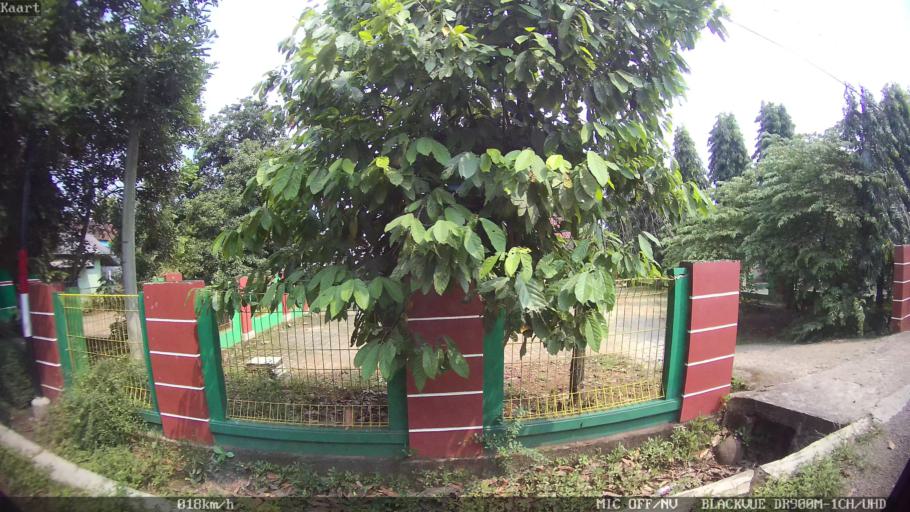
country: ID
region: Lampung
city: Gadingrejo
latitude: -5.3622
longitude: 105.0436
